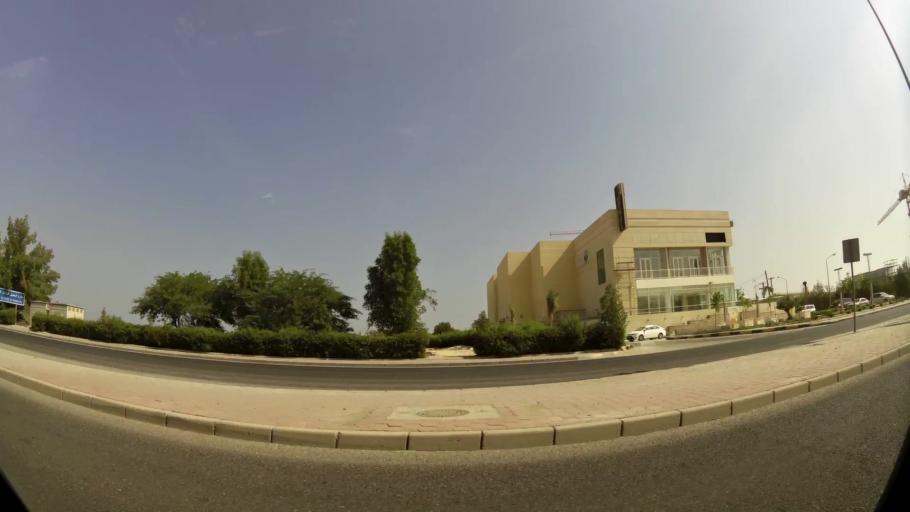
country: KW
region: Al Ahmadi
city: Al Mahbulah
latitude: 29.1241
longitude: 48.1332
